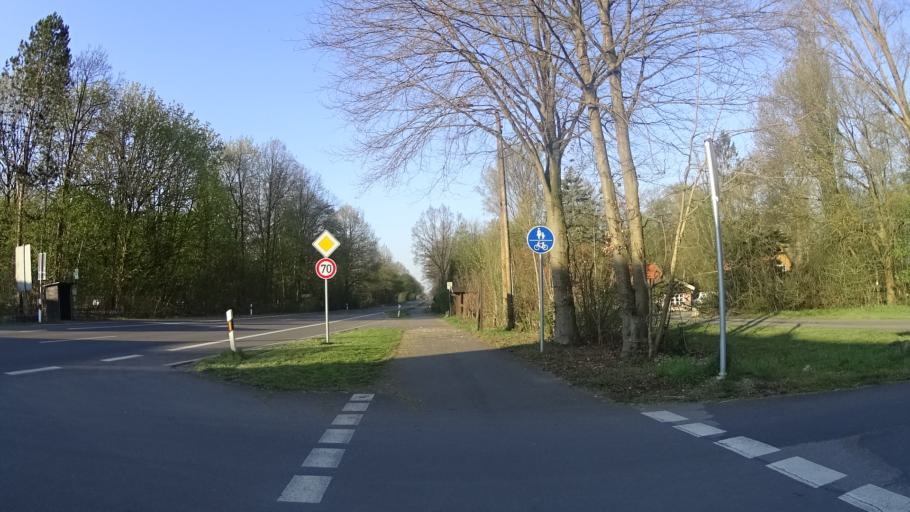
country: DE
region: North Rhine-Westphalia
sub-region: Regierungsbezirk Dusseldorf
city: Hunxe
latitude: 51.6609
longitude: 6.8089
